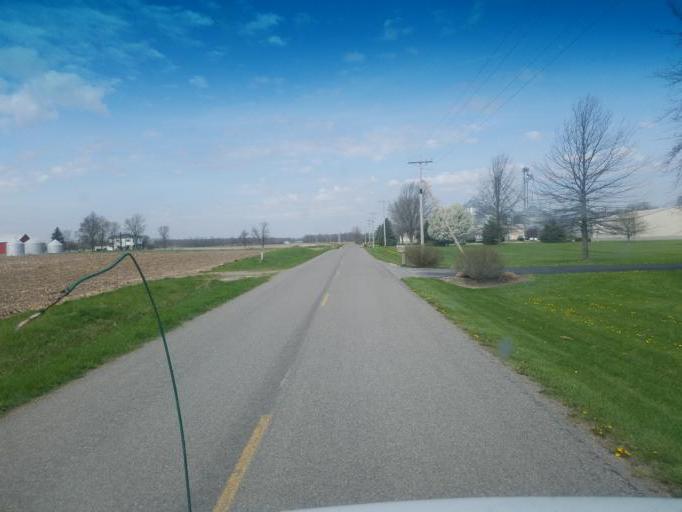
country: US
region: Ohio
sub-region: Logan County
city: Northwood
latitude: 40.4947
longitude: -83.6063
